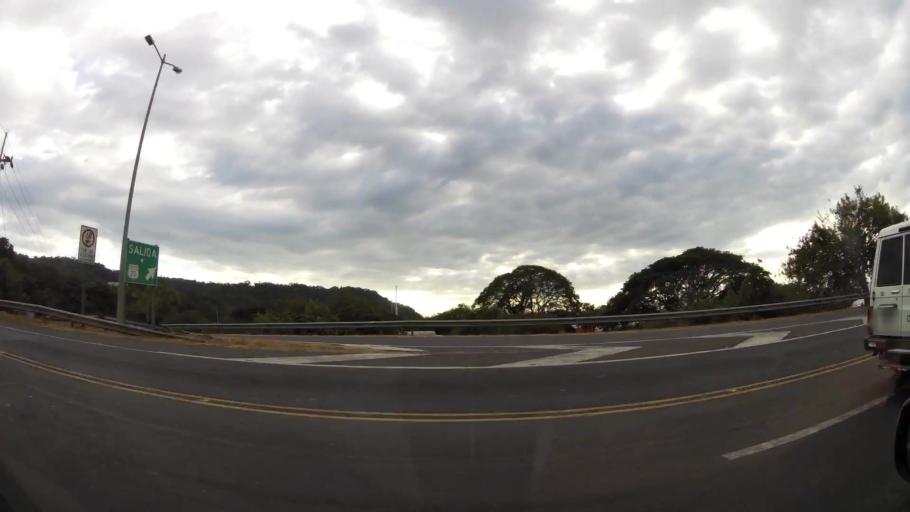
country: CR
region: Puntarenas
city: Esparza
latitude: 9.9171
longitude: -84.7117
